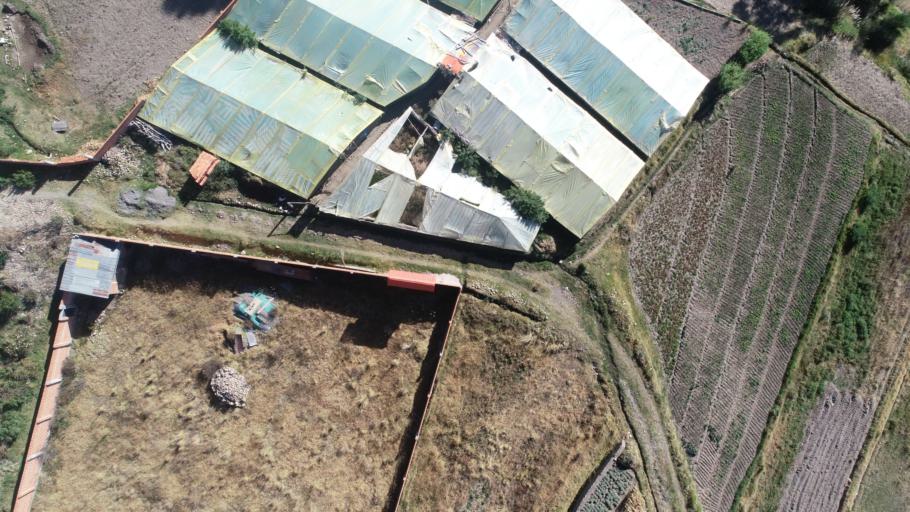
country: BO
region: La Paz
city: La Paz
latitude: -16.4867
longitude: -68.0848
